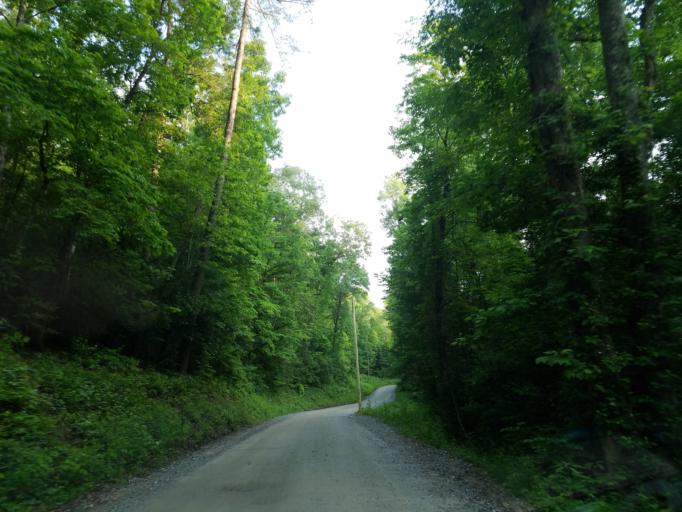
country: US
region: Georgia
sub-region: Dawson County
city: Dawsonville
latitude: 34.5711
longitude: -84.1358
